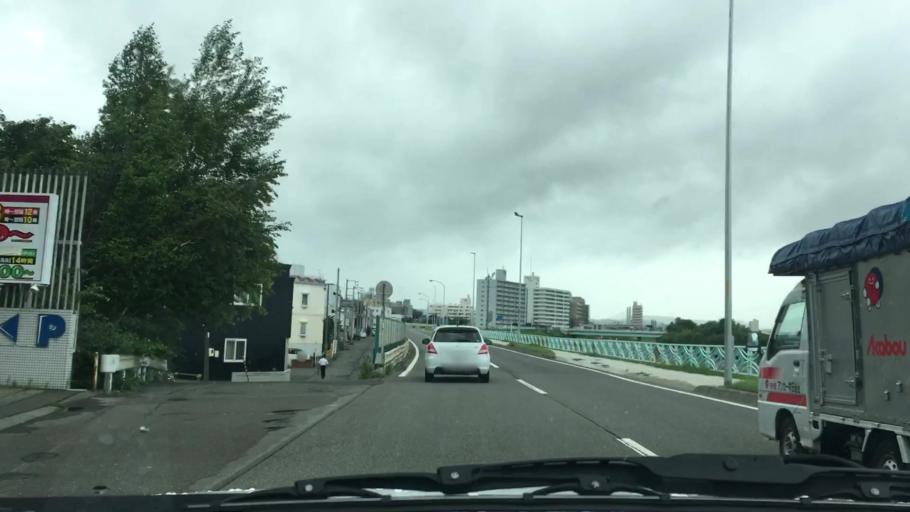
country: JP
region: Hokkaido
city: Sapporo
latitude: 43.0342
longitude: 141.3570
